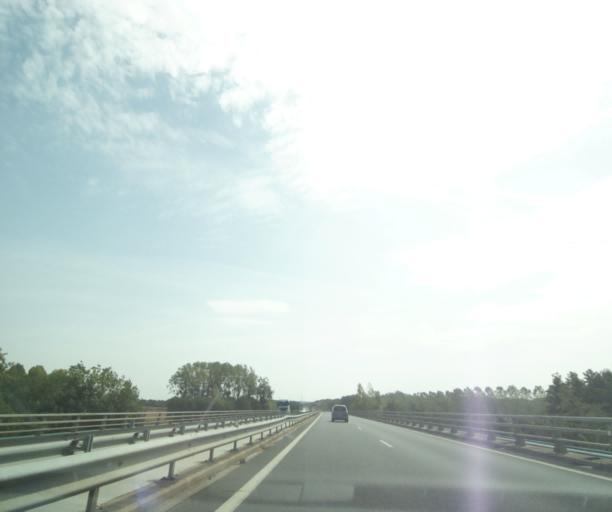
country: FR
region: Poitou-Charentes
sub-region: Departement des Deux-Sevres
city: Chauray
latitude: 46.3769
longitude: -0.3606
